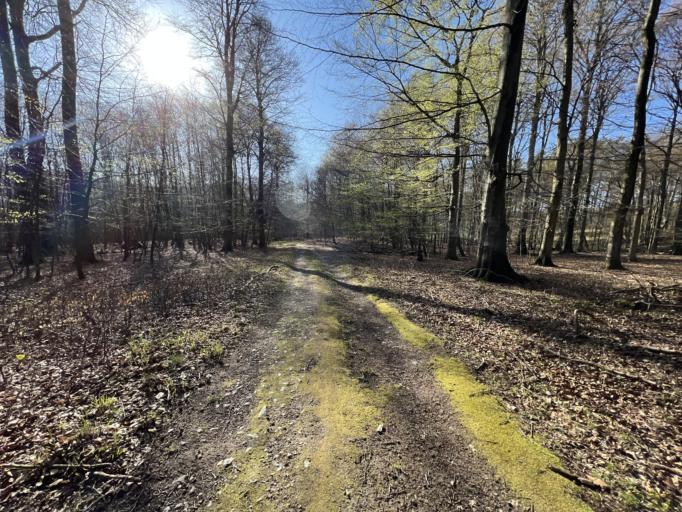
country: DE
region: Mecklenburg-Vorpommern
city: Sassnitz
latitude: 54.5400
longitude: 13.6293
